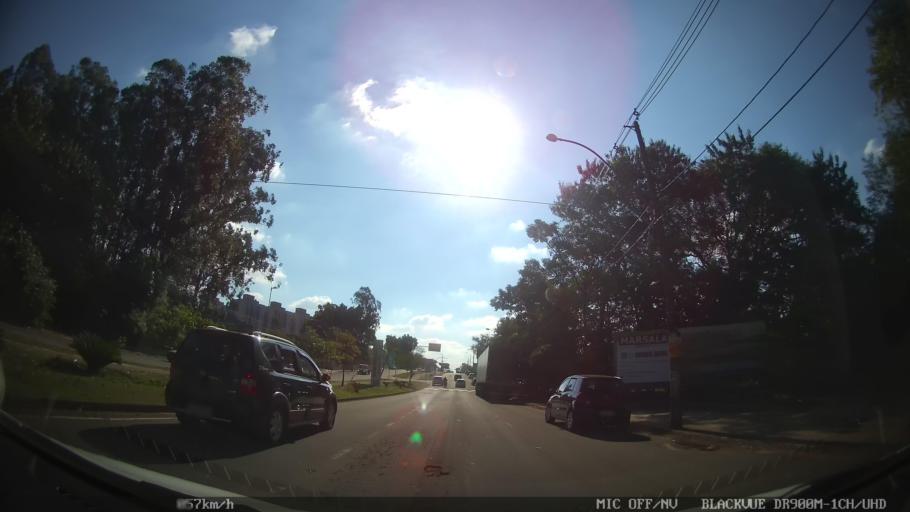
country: BR
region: Sao Paulo
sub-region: Sumare
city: Sumare
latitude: -22.8039
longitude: -47.2861
